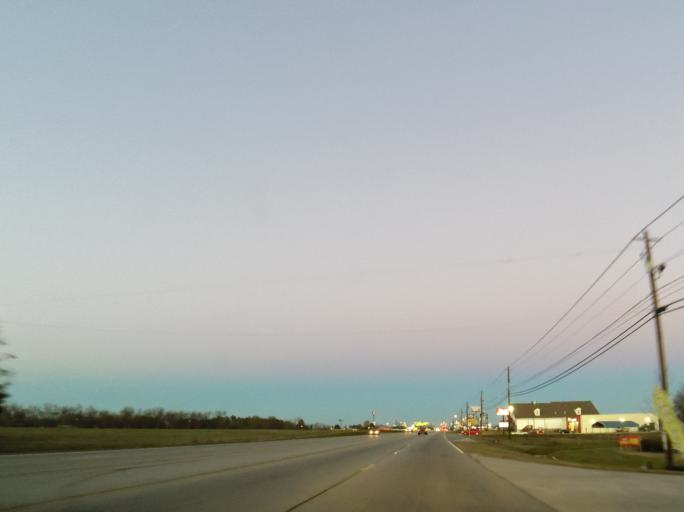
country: US
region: Georgia
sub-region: Peach County
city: Byron
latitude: 32.6546
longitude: -83.7524
